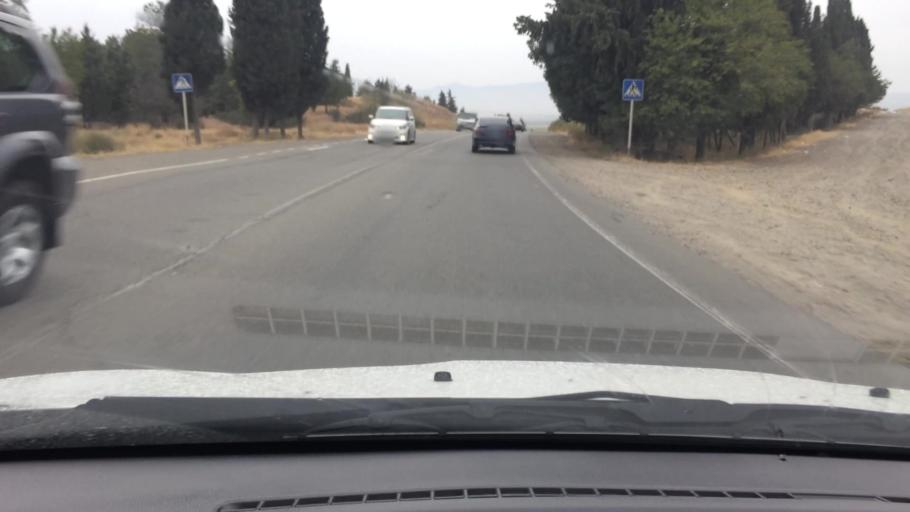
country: GE
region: Kvemo Kartli
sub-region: Marneuli
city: Marneuli
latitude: 41.5221
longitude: 44.7790
